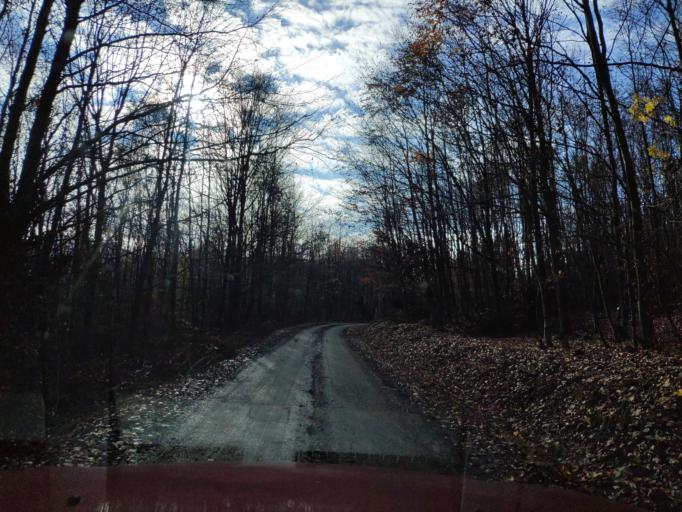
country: HU
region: Borsod-Abauj-Zemplen
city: Gonc
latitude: 48.6063
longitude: 21.4572
